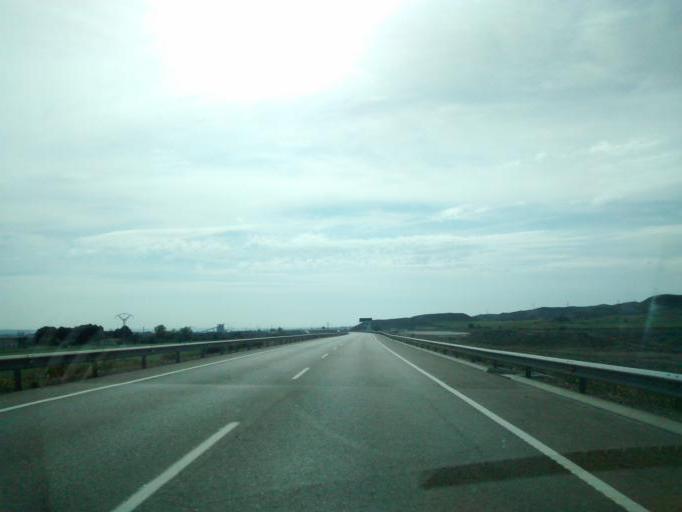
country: ES
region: Aragon
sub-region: Provincia de Zaragoza
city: El Burgo de Ebro
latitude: 41.5519
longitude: -0.7125
